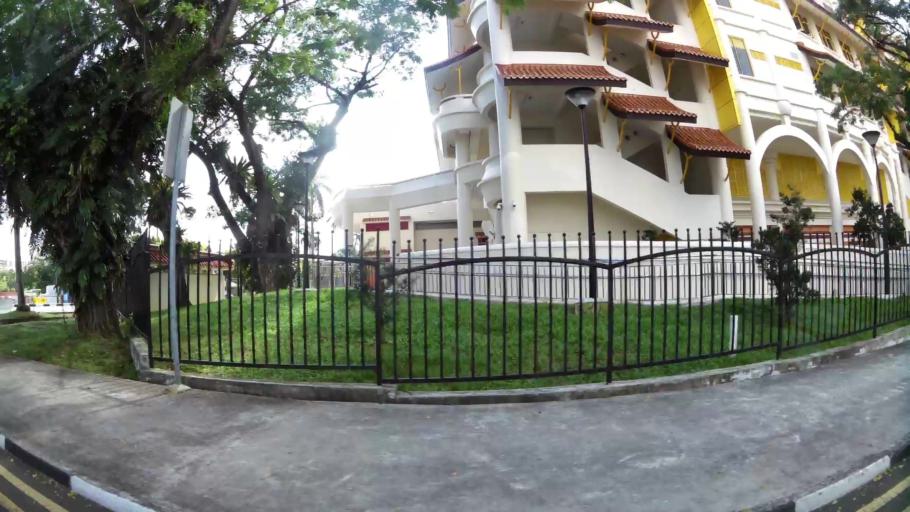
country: SG
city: Singapore
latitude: 1.3630
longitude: 103.8360
